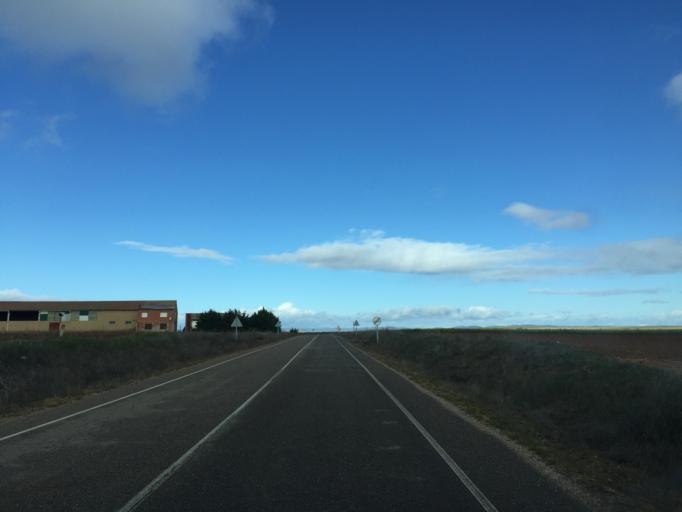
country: ES
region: Castille and Leon
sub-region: Provincia de Zamora
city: Manganeses de la Lampreana
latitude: 41.7562
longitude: -5.7206
